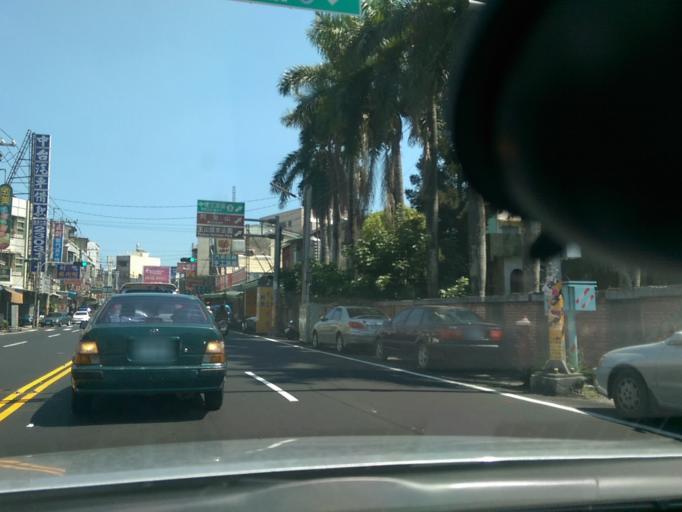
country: TW
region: Taiwan
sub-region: Chiayi
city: Jiayi Shi
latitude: 23.4504
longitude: 120.4598
